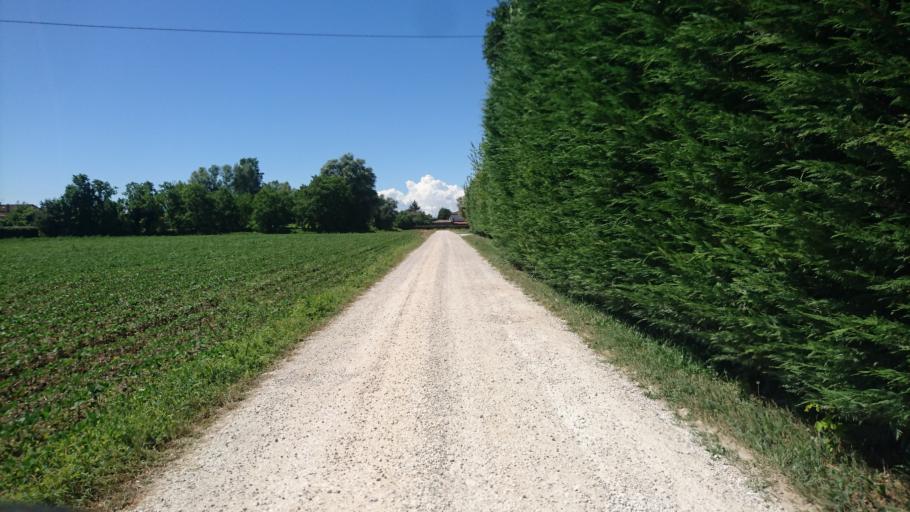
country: IT
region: Veneto
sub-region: Provincia di Padova
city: Pontelongo
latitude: 45.2534
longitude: 12.0177
